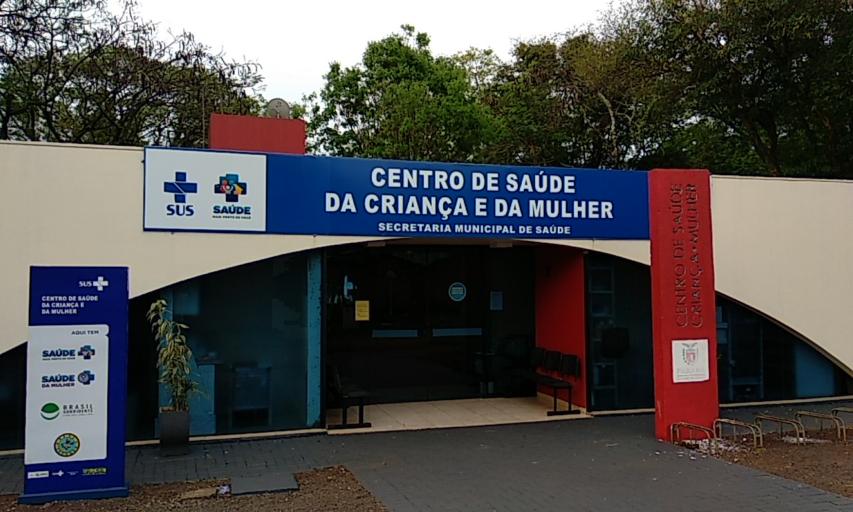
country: BR
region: Parana
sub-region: Marechal Candido Rondon
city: Marechal Candido Rondon
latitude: -24.5582
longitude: -54.0580
